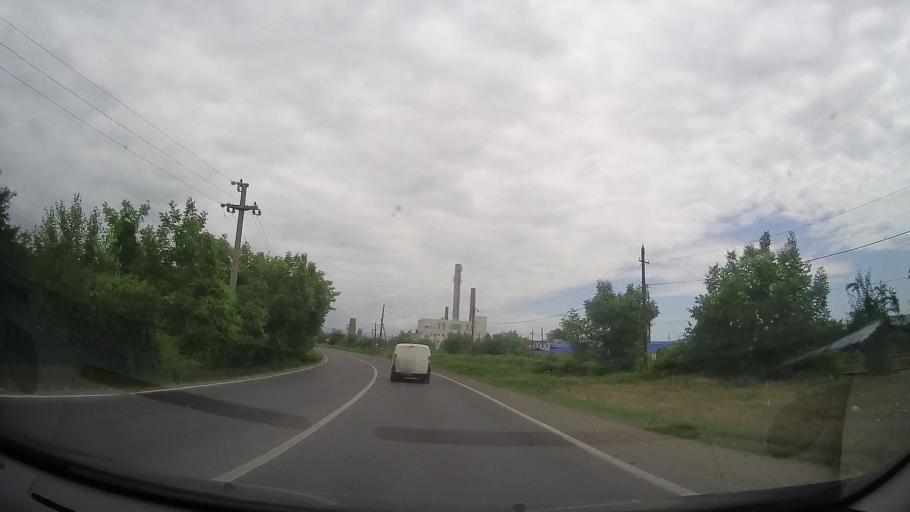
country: RO
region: Prahova
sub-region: Comuna Blejoiu
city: Ploiestiori
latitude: 44.9889
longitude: 26.0155
